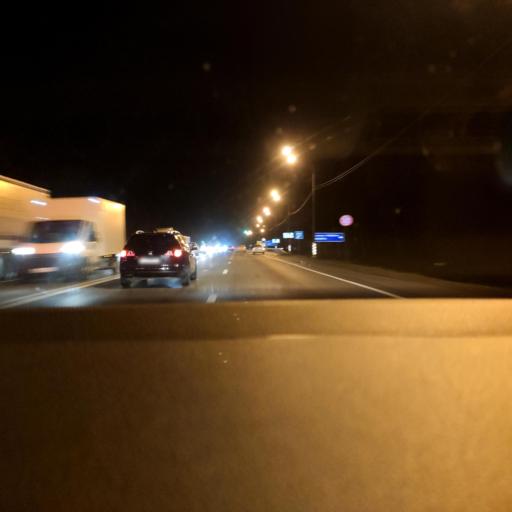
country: RU
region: Moskovskaya
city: Kievskij
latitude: 55.4168
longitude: 36.8383
